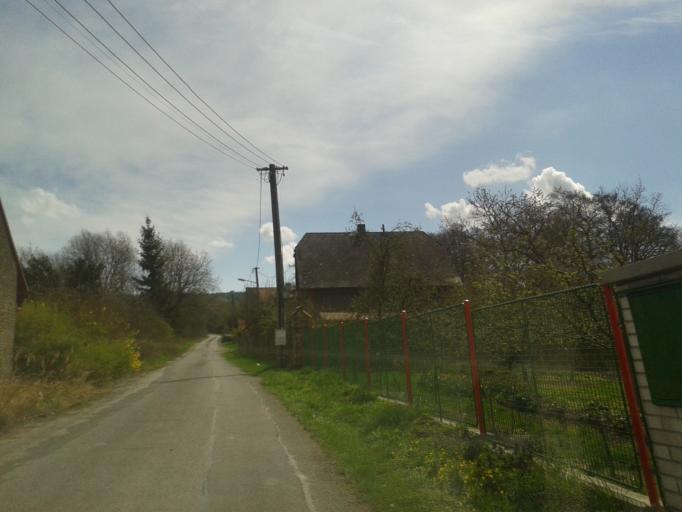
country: CZ
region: Central Bohemia
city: Dobris
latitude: 49.8685
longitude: 14.1420
